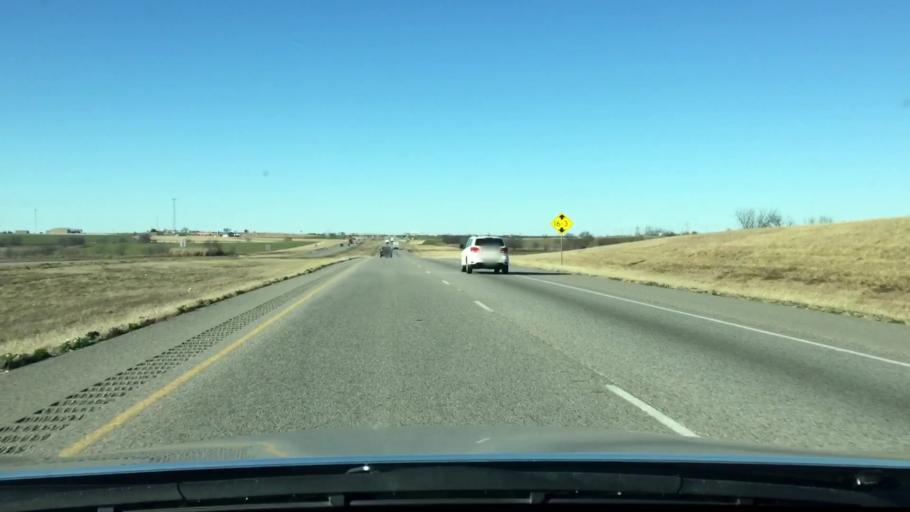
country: US
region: Texas
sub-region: Hill County
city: Itasca
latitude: 32.1426
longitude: -97.1228
